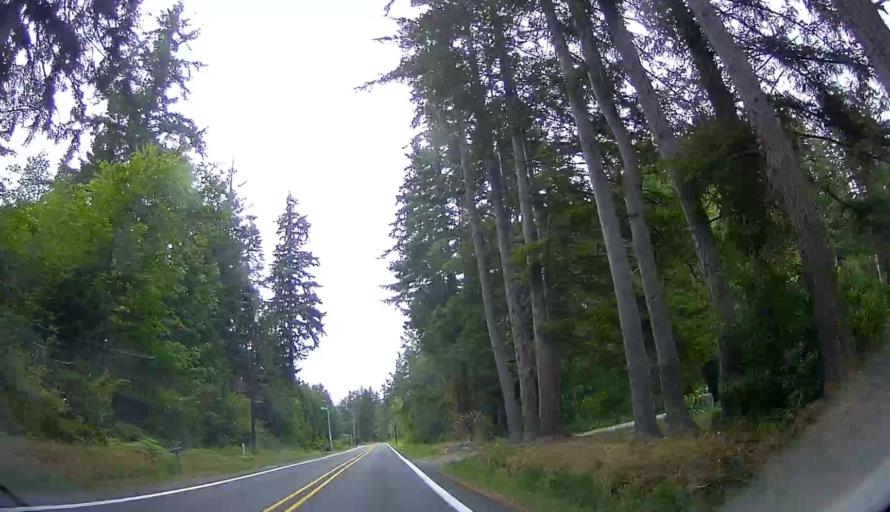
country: US
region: Washington
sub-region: Snohomish County
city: Warm Beach
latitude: 48.1496
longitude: -122.3603
